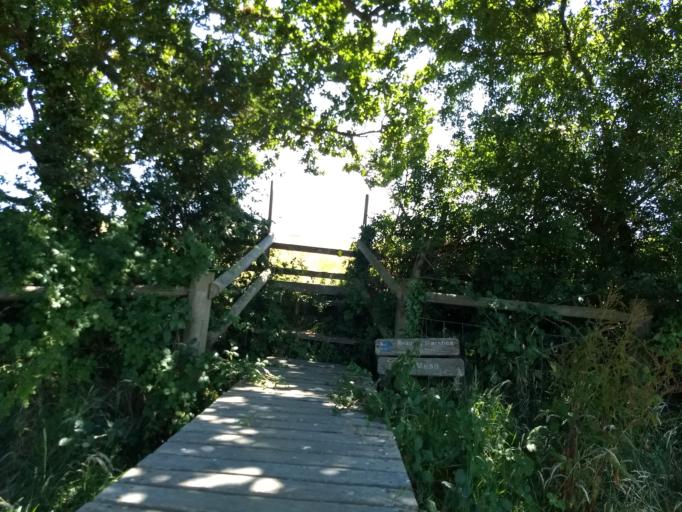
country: GB
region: England
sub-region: Isle of Wight
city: Brading
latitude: 50.6671
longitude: -1.1395
